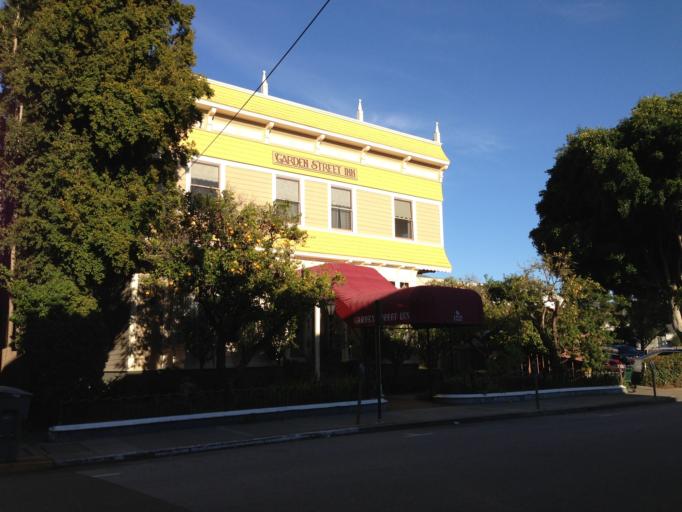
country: US
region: California
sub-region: San Luis Obispo County
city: San Luis Obispo
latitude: 35.2785
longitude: -120.6627
